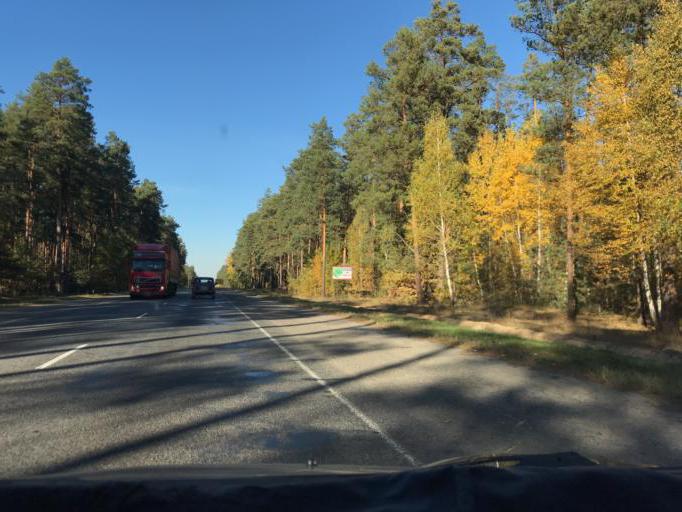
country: BY
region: Gomel
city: Kalinkavichy
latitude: 52.0601
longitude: 29.3611
